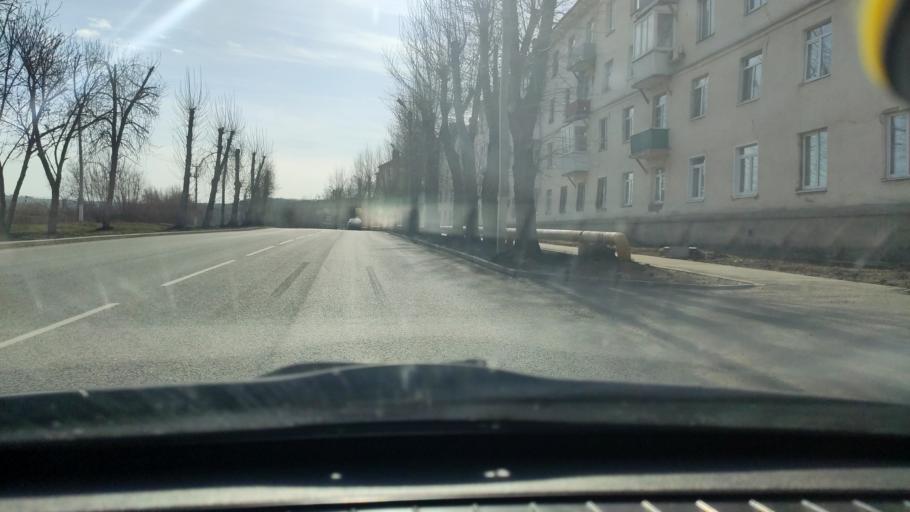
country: RU
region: Samara
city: Zhigulevsk
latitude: 53.4047
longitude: 49.4952
